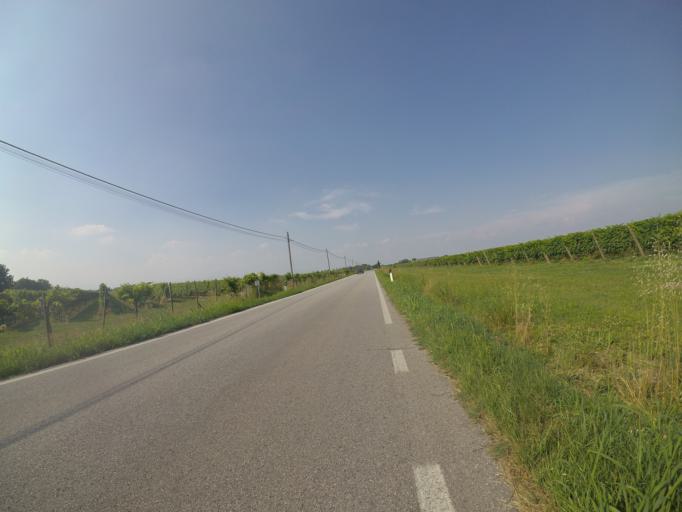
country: IT
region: Friuli Venezia Giulia
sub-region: Provincia di Udine
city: Camino al Tagliamento
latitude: 45.9325
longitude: 12.9584
